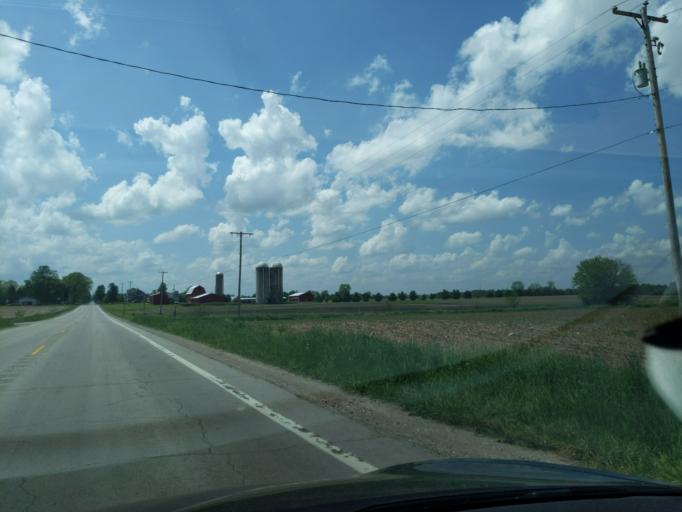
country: US
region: Michigan
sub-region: Ingham County
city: Williamston
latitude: 42.5559
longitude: -84.2822
